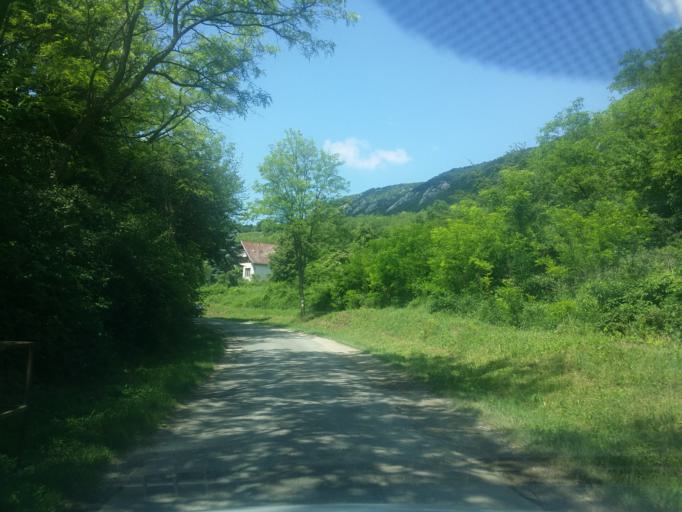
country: HU
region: Komarom-Esztergom
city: Kesztolc
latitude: 47.7131
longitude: 18.8138
